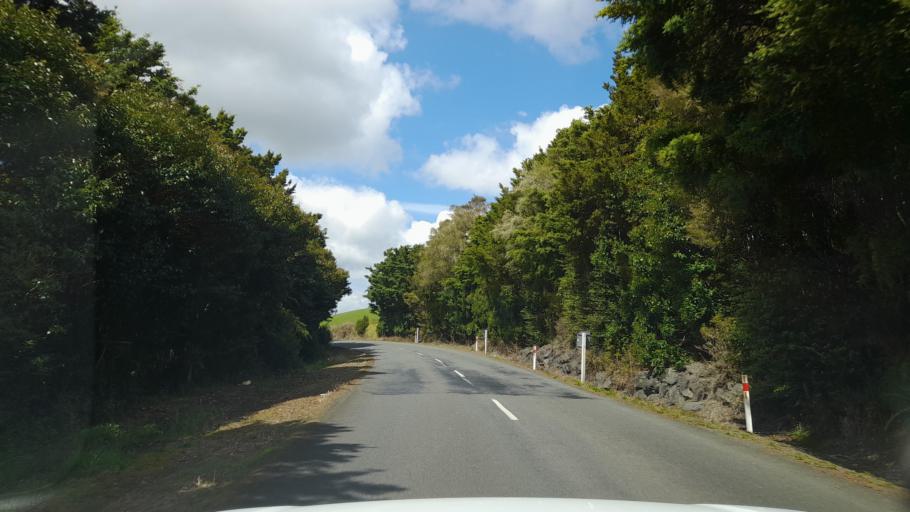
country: NZ
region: Northland
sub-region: Whangarei
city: Maungatapere
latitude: -35.6388
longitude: 174.0662
